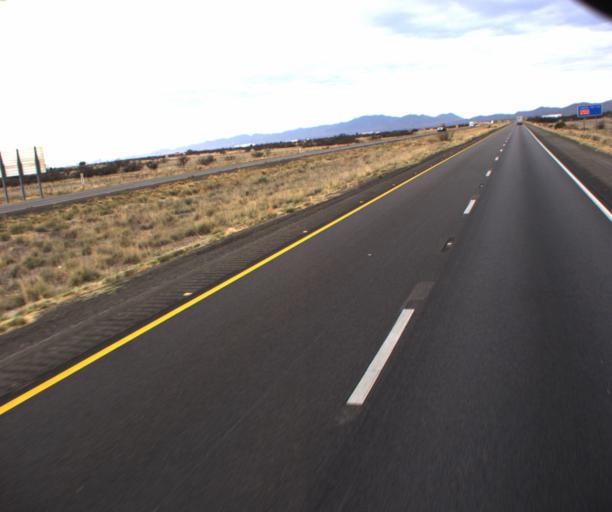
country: US
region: Arizona
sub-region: Cochise County
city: Willcox
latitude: 32.2362
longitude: -109.8676
